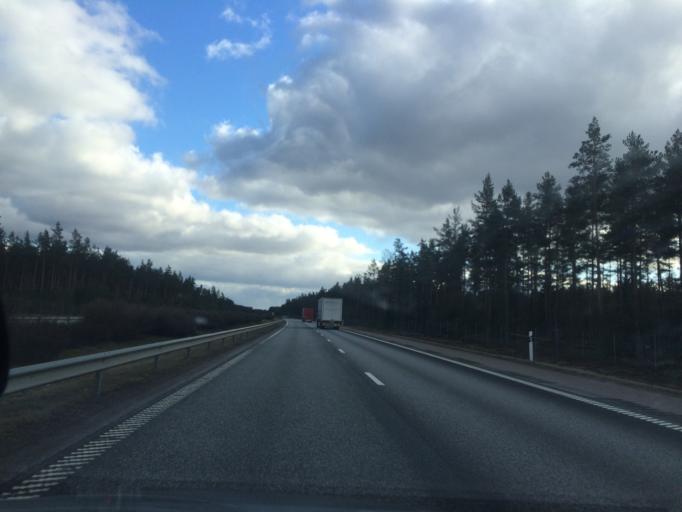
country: SE
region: Joenkoeping
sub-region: Vaggeryds Kommun
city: Skillingaryd
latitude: 57.3771
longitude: 14.1006
